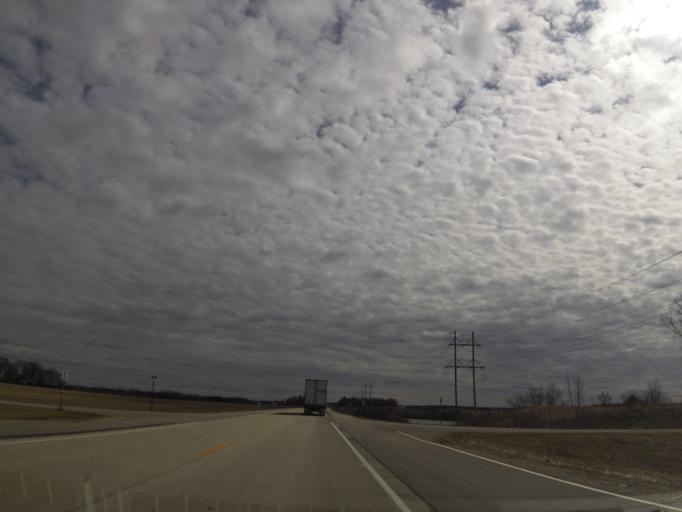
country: US
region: Minnesota
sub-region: Fillmore County
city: Spring Valley
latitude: 43.6460
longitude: -92.3894
